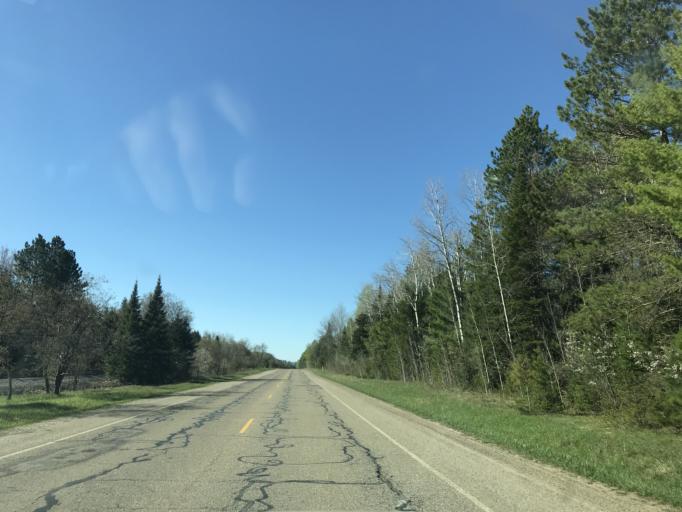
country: US
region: Michigan
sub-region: Crawford County
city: Grayling
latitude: 44.7464
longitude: -84.7513
